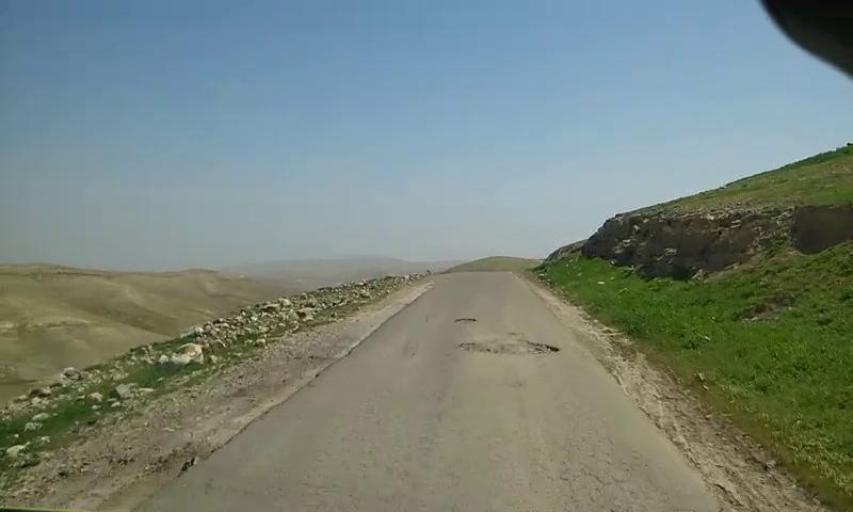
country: PS
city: `Arab ar Rashaydah
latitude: 31.5428
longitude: 35.2615
